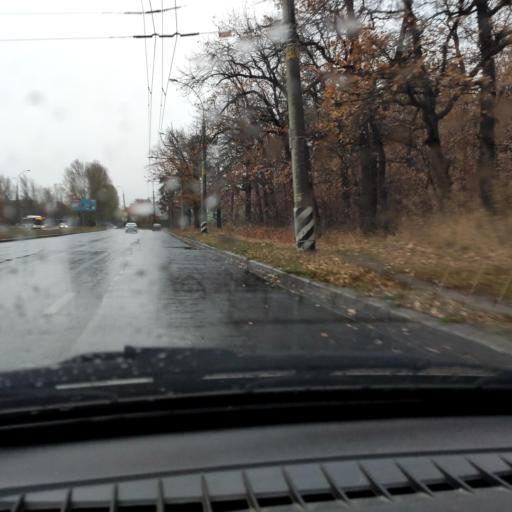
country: RU
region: Samara
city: Tol'yatti
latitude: 53.4979
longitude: 49.2967
